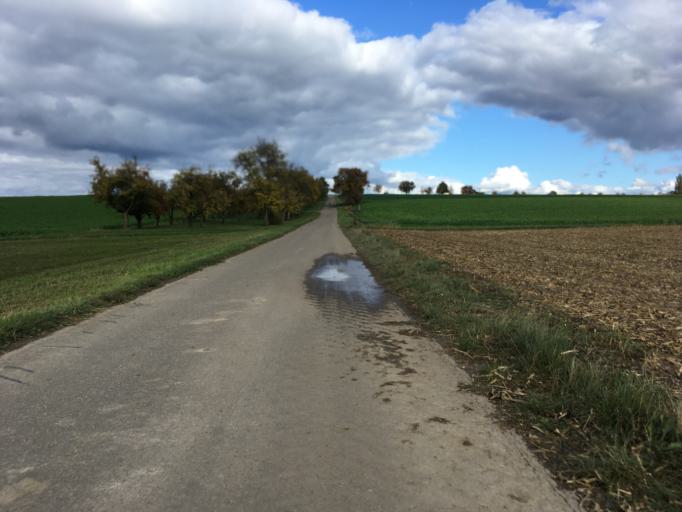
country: DE
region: Baden-Wuerttemberg
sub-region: Regierungsbezirk Stuttgart
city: Untermunkheim
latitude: 49.1824
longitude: 9.7079
